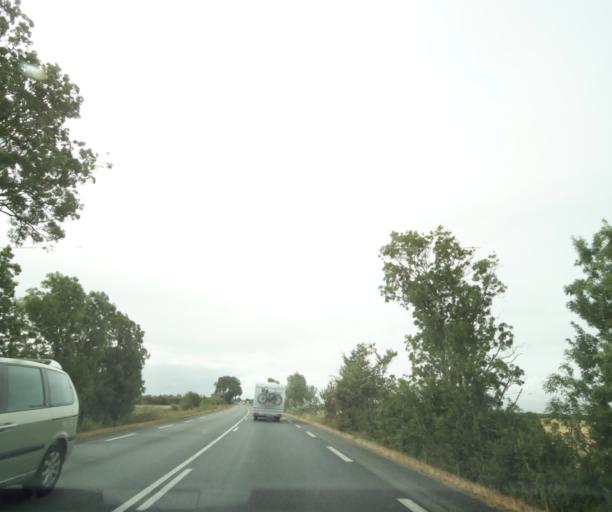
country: FR
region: Pays de la Loire
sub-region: Departement de la Vendee
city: Sainte-Gemme-la-Plaine
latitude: 46.4322
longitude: -1.0974
